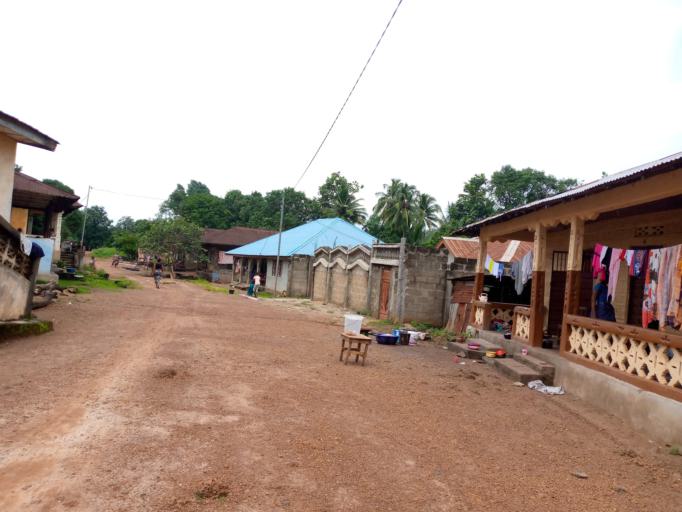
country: SL
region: Northern Province
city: Magburaka
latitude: 8.7201
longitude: -11.9406
